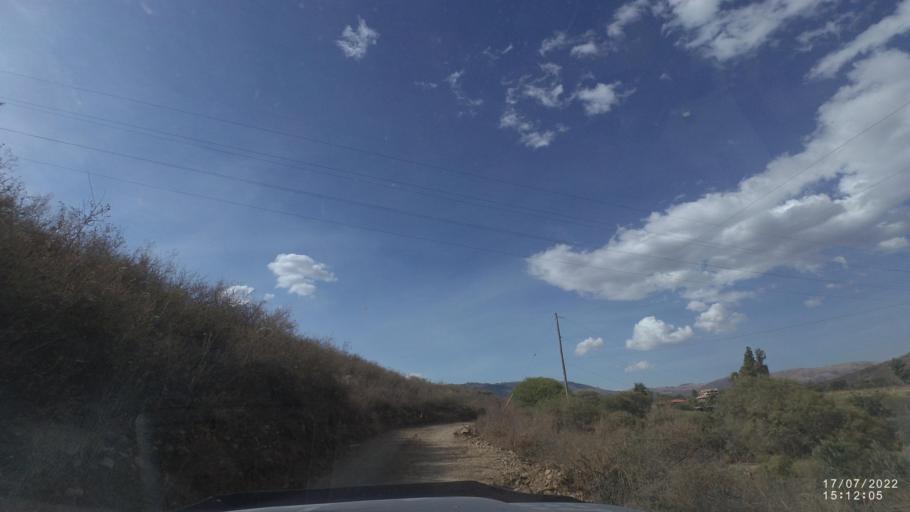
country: BO
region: Cochabamba
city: Capinota
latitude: -17.5712
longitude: -66.2646
